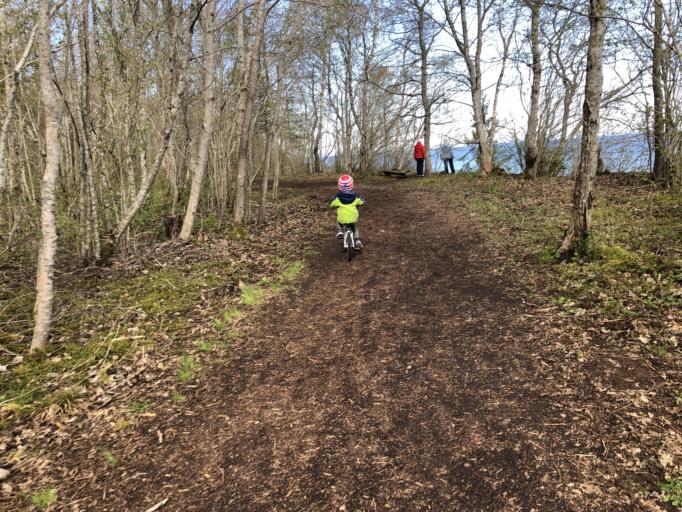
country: EE
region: Harju
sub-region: Harku vald
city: Tabasalu
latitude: 59.4398
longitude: 24.5332
